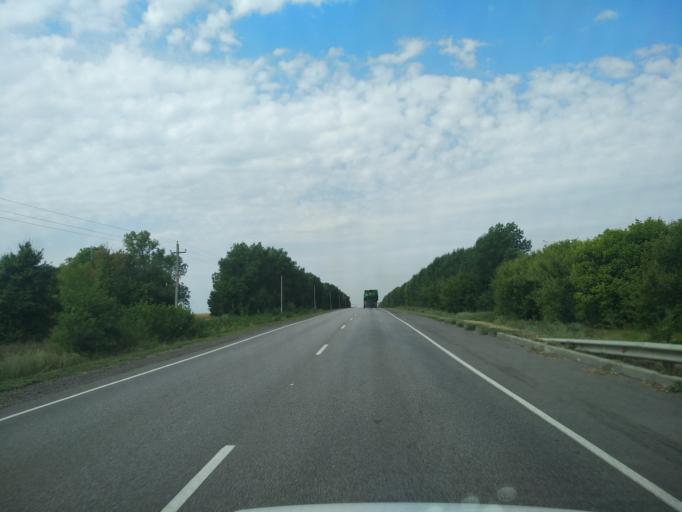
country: RU
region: Lipetsk
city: Dobrinka
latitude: 51.8919
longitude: 40.4429
